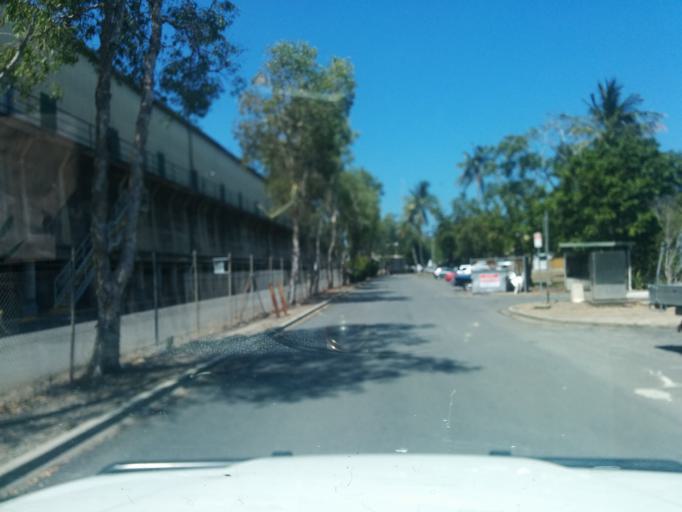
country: AU
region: Queensland
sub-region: Cairns
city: Cairns
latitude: -16.9406
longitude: 145.7763
